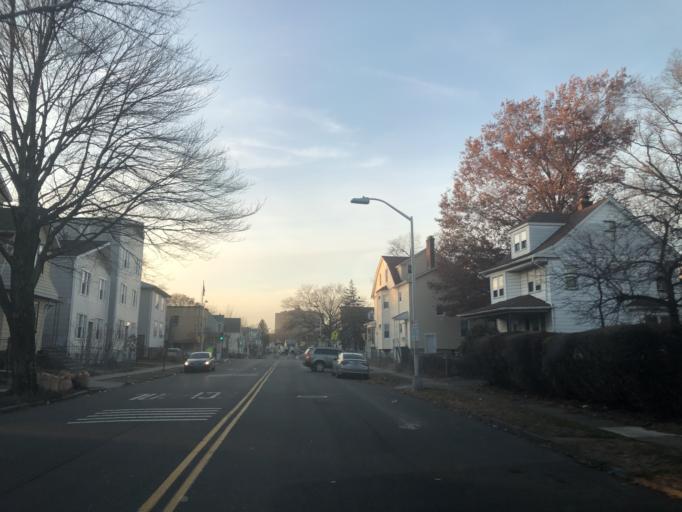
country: US
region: New Jersey
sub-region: Essex County
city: Orange
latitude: 40.7544
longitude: -74.2214
